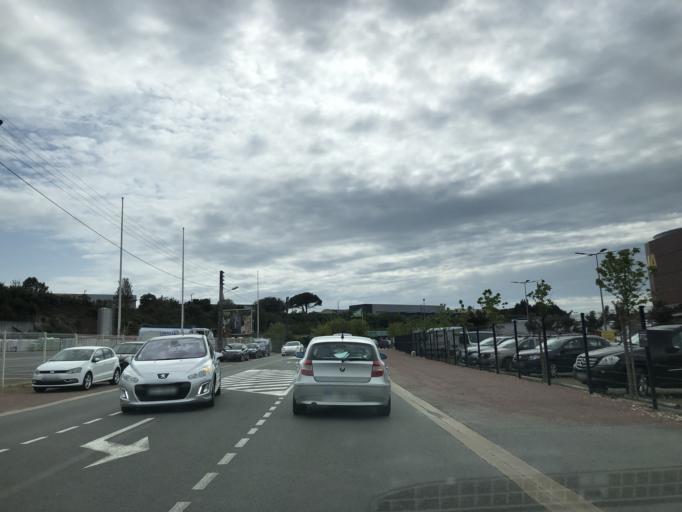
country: FR
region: Poitou-Charentes
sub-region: Departement de la Charente-Maritime
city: Saint-Georges-de-Didonne
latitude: 45.6312
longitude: -0.9972
